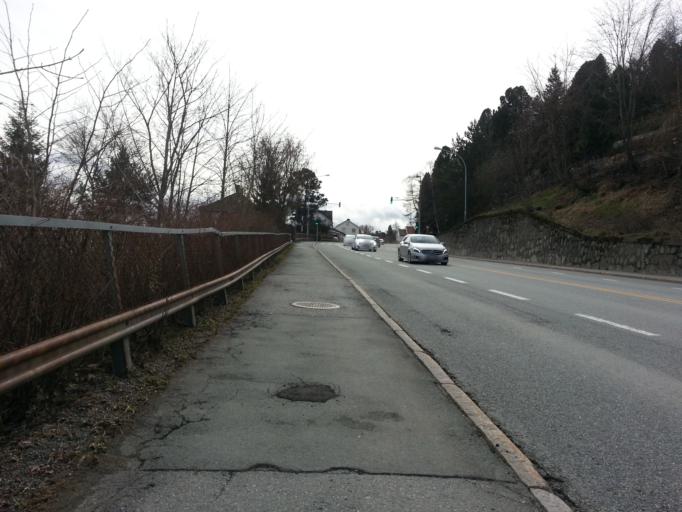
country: NO
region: Sor-Trondelag
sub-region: Trondheim
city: Trondheim
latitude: 63.4221
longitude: 10.3727
